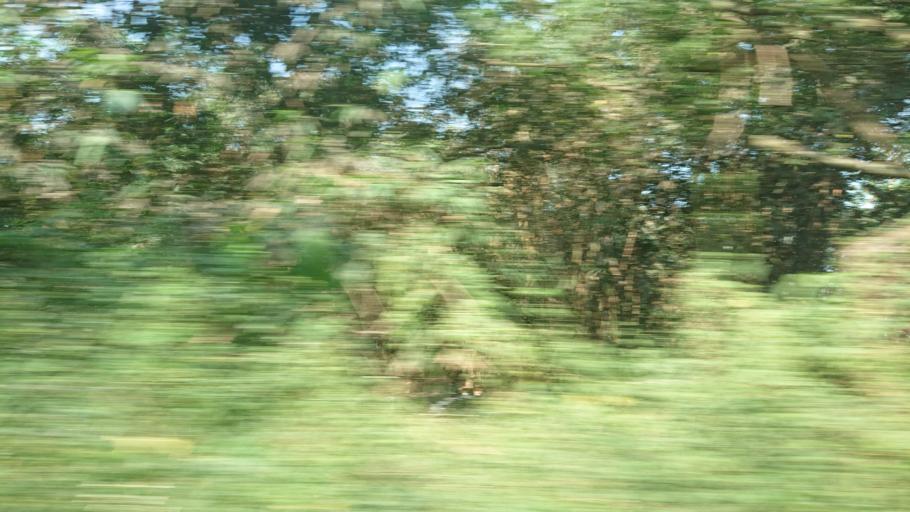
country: TW
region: Taiwan
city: Lugu
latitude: 23.7193
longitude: 120.6696
